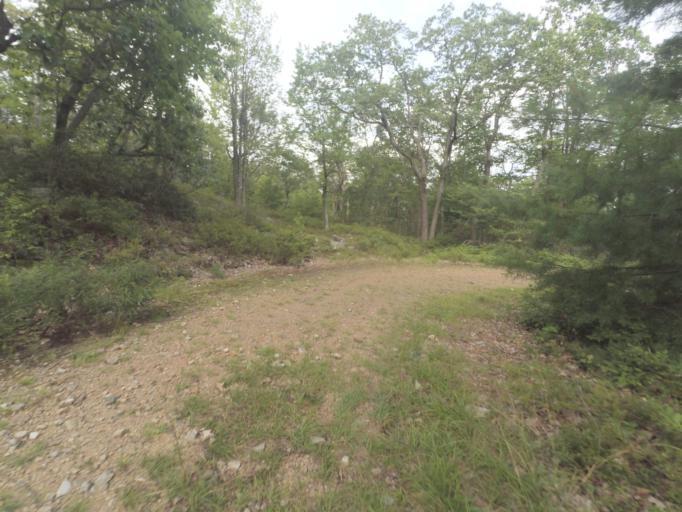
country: US
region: Pennsylvania
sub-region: Centre County
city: Boalsburg
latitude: 40.7177
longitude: -77.7773
